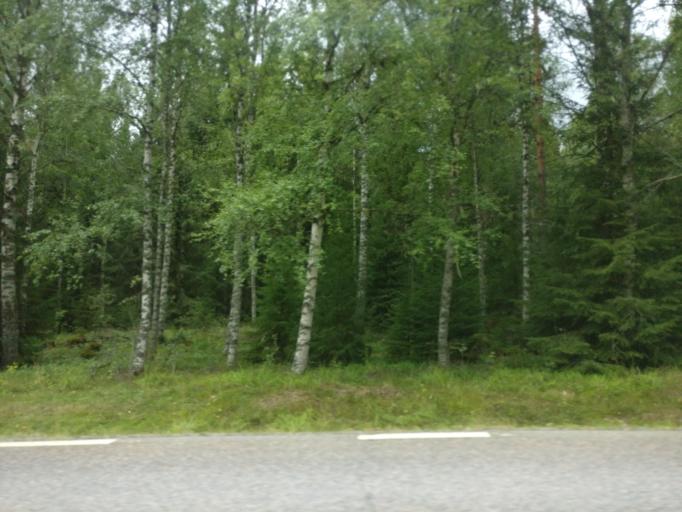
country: SE
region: Vaermland
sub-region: Torsby Kommun
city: Torsby
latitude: 60.7624
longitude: 12.7627
